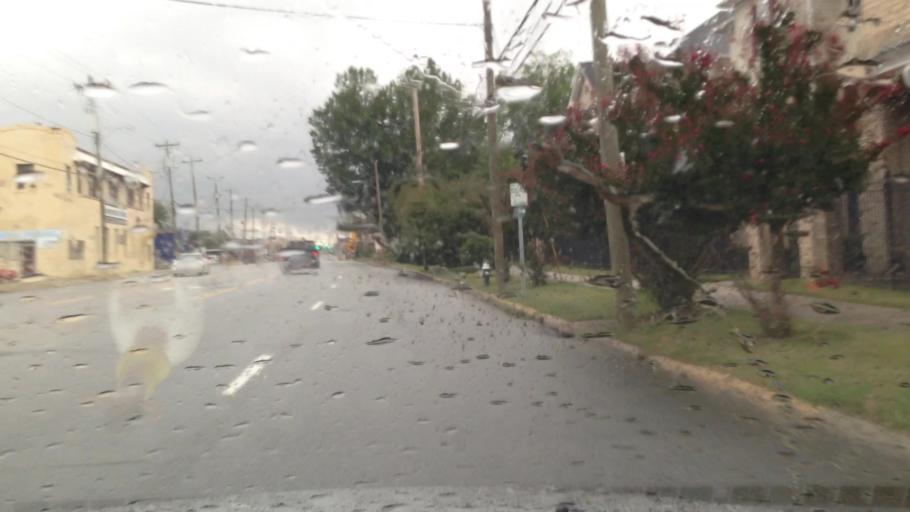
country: US
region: North Carolina
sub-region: Guilford County
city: Greensboro
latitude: 36.0640
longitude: -79.8017
